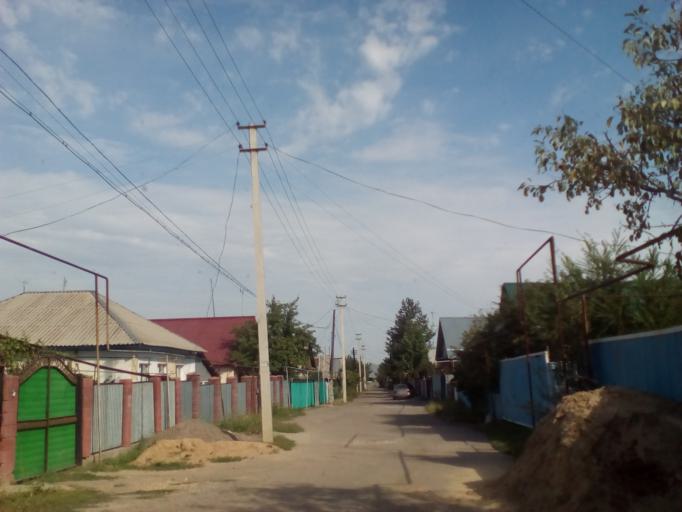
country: KZ
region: Almaty Oblysy
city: Burunday
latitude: 43.1615
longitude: 76.4079
